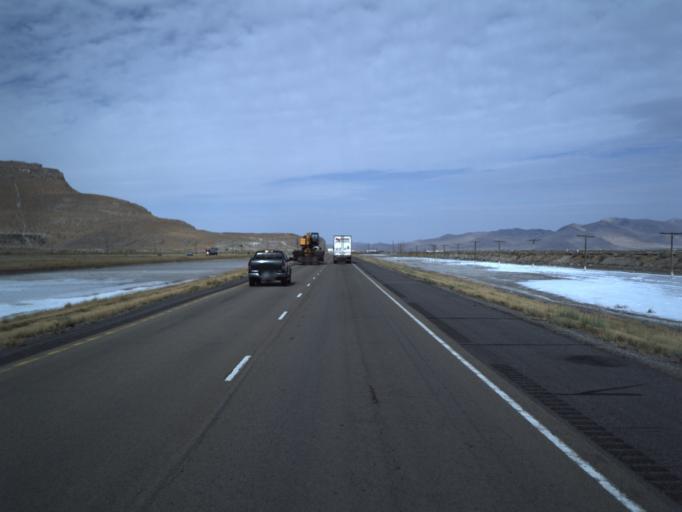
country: US
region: Utah
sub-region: Tooele County
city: Grantsville
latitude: 40.7371
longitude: -112.6116
